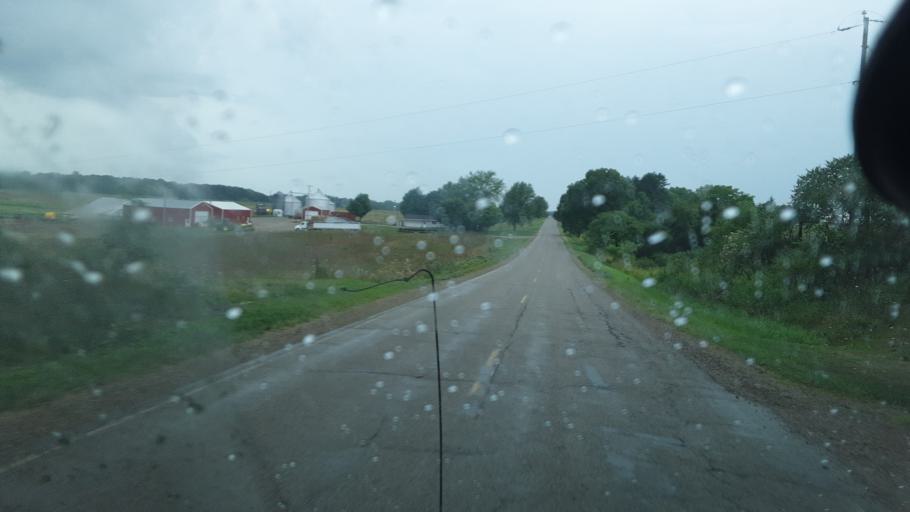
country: US
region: Michigan
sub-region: Hillsdale County
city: Reading
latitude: 41.7081
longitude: -84.7278
